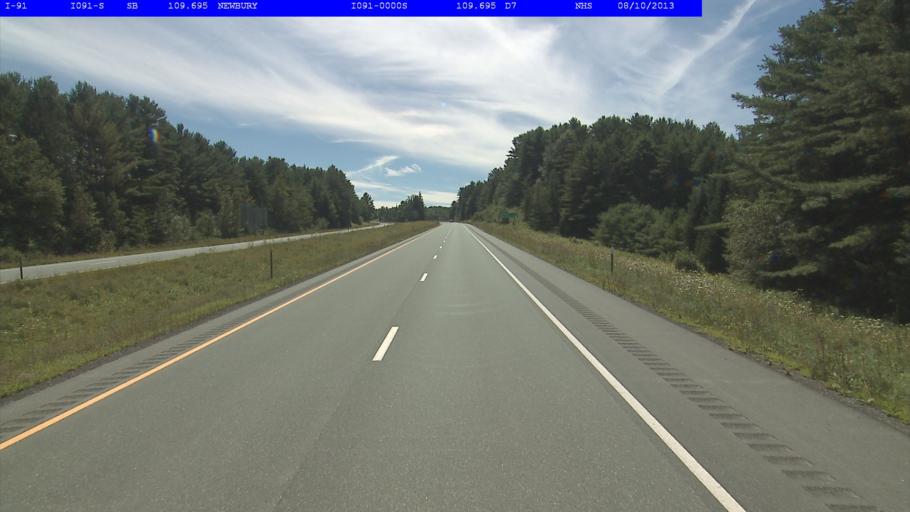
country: US
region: New Hampshire
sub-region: Grafton County
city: Woodsville
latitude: 44.1521
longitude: -72.0956
